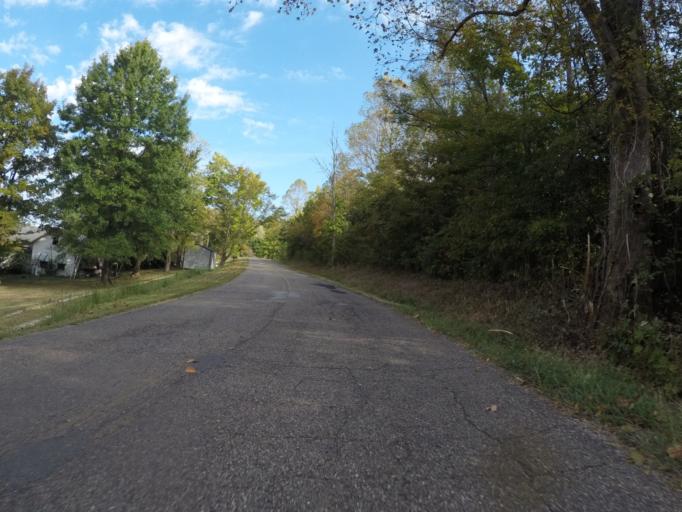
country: US
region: West Virginia
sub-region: Cabell County
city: Lesage
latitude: 38.5909
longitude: -82.4225
